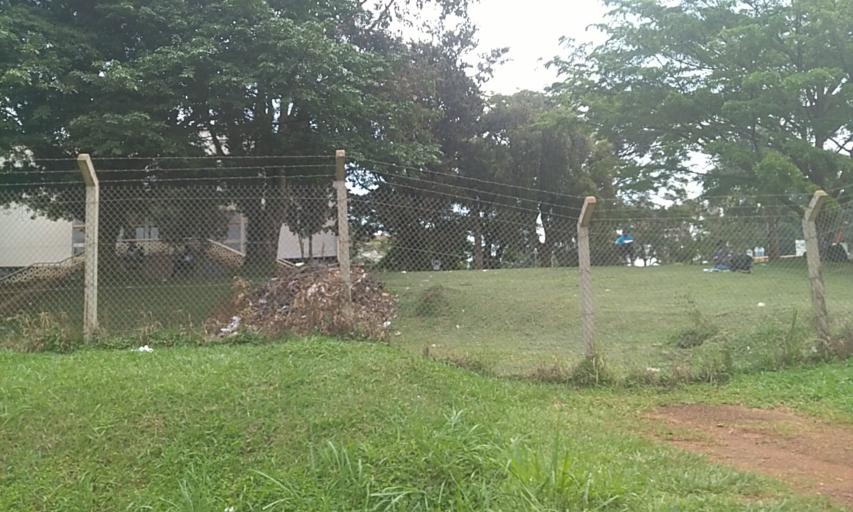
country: UG
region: Central Region
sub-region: Wakiso District
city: Kireka
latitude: 0.3480
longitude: 32.6253
